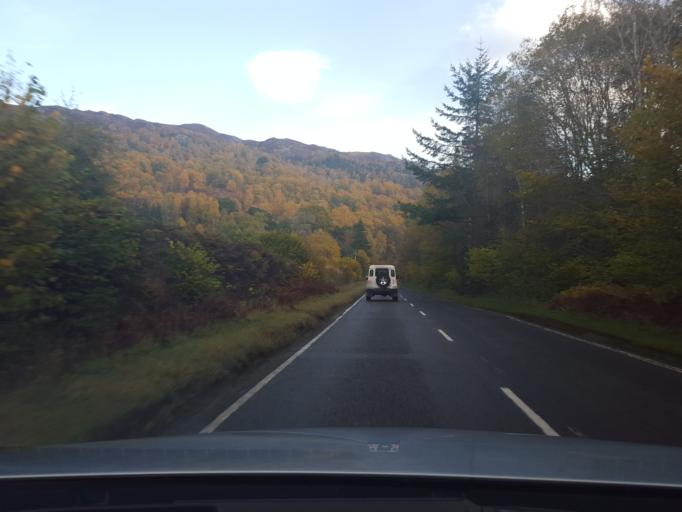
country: GB
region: Scotland
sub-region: Highland
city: Beauly
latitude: 57.2194
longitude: -4.6504
